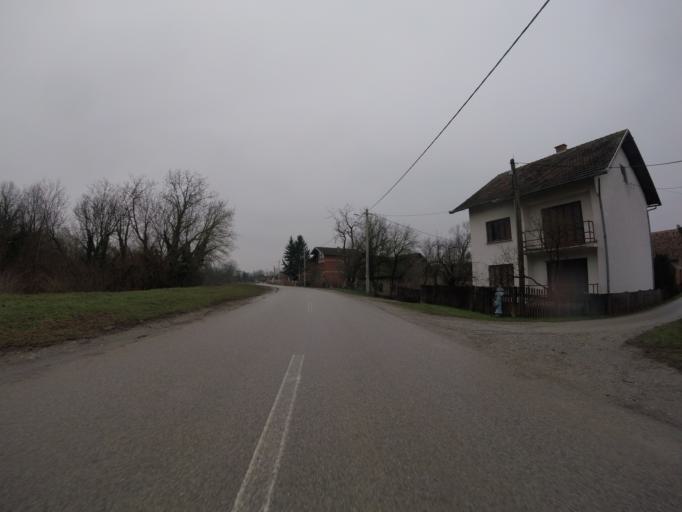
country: HR
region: Sisacko-Moslavacka
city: Lekenik
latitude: 45.6177
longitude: 16.3296
